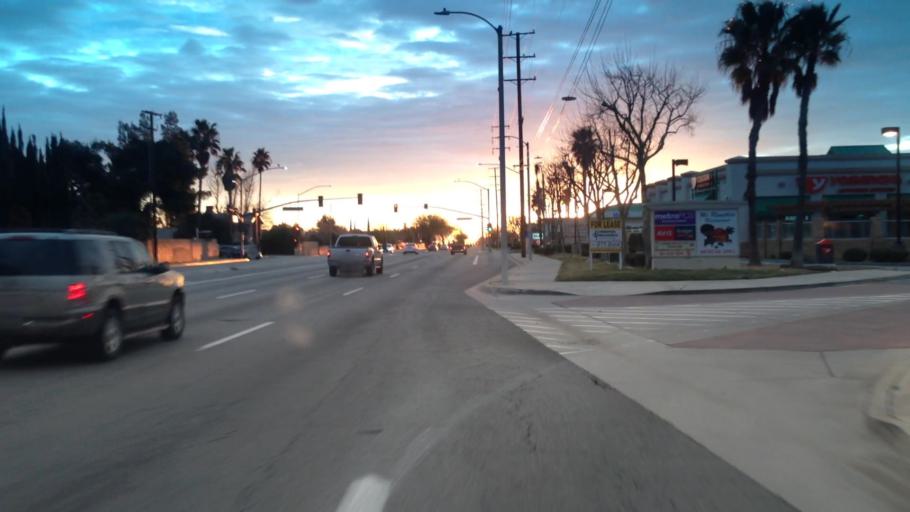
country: US
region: California
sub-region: Los Angeles County
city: Desert View Highlands
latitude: 34.6016
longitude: -118.1407
